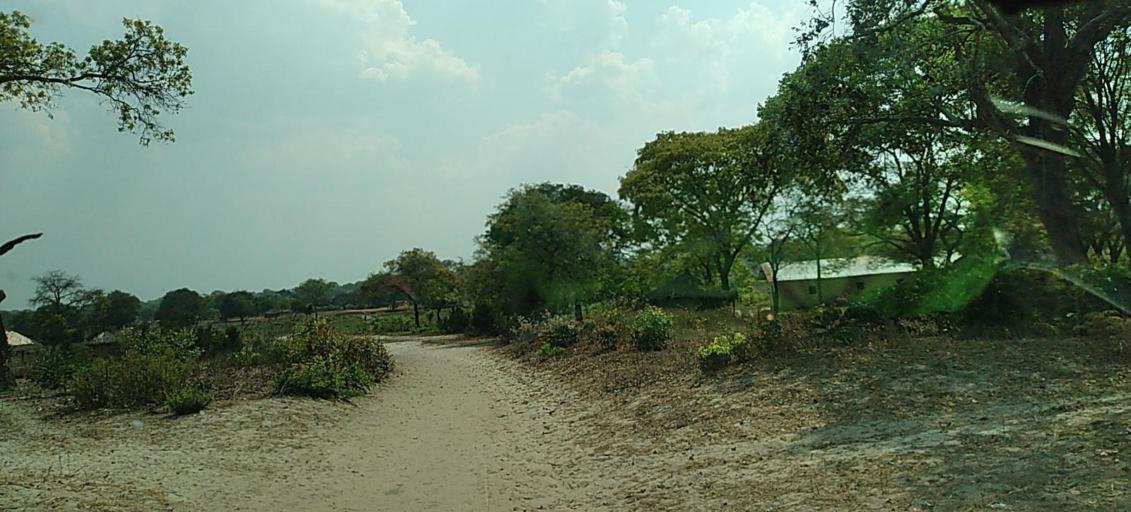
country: ZM
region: North-Western
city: Kabompo
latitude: -13.4469
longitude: 23.6655
